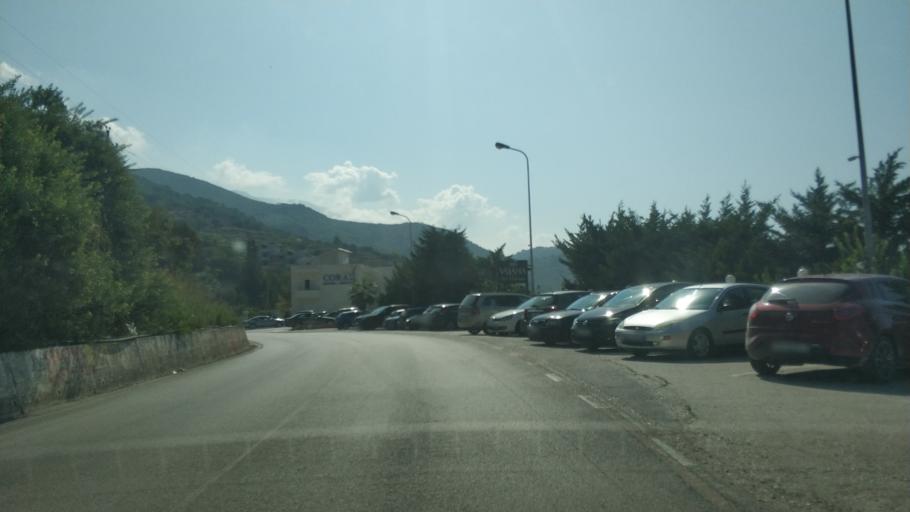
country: AL
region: Vlore
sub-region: Rrethi i Vlores
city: Orikum
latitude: 40.3923
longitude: 19.4798
